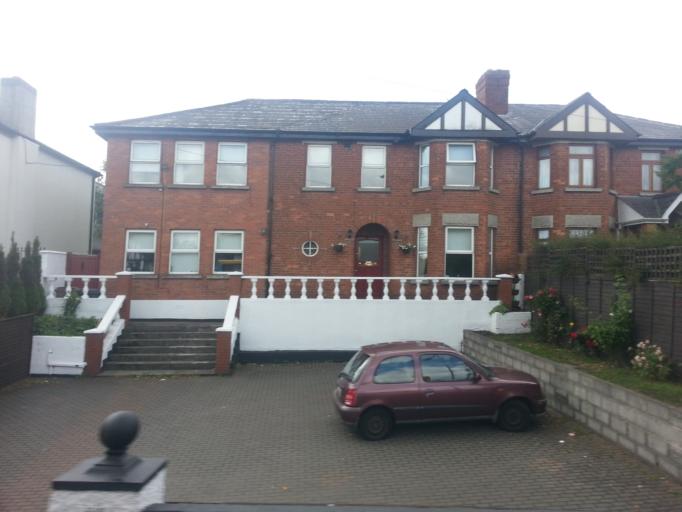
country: IE
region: Leinster
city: Cabra
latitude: 53.3595
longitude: -6.2931
